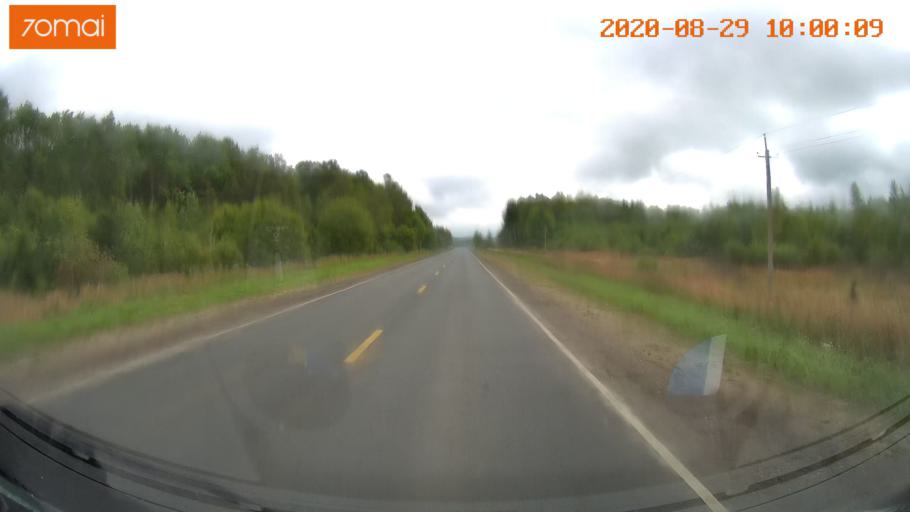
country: RU
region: Ivanovo
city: Zarechnyy
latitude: 57.4100
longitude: 42.3854
